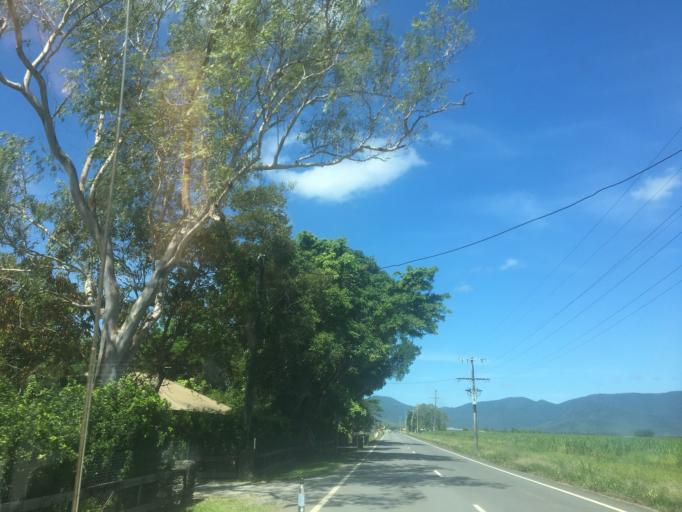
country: AU
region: Queensland
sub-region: Cairns
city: Woree
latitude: -17.0627
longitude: 145.7593
